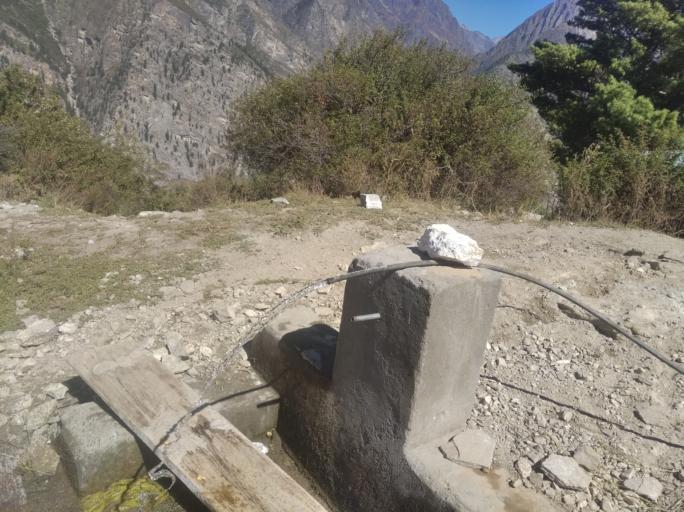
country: NP
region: Western Region
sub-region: Dhawalagiri Zone
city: Jomsom
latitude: 28.8905
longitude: 83.0577
